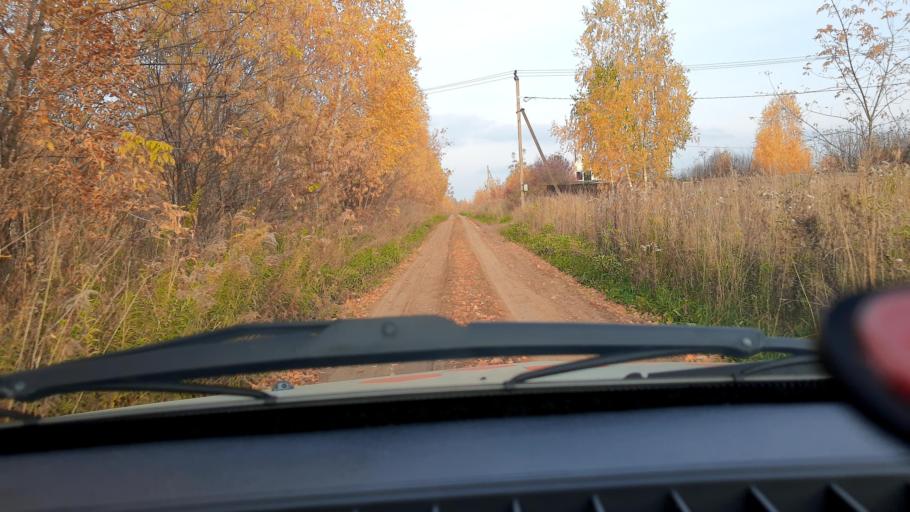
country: RU
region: Bashkortostan
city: Iglino
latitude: 54.8064
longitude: 56.3476
